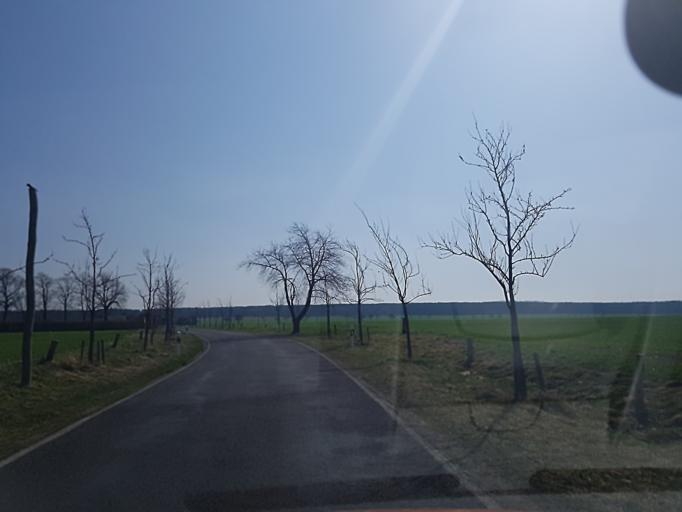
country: DE
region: Saxony
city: Gross Duben
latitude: 51.6678
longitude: 14.5447
